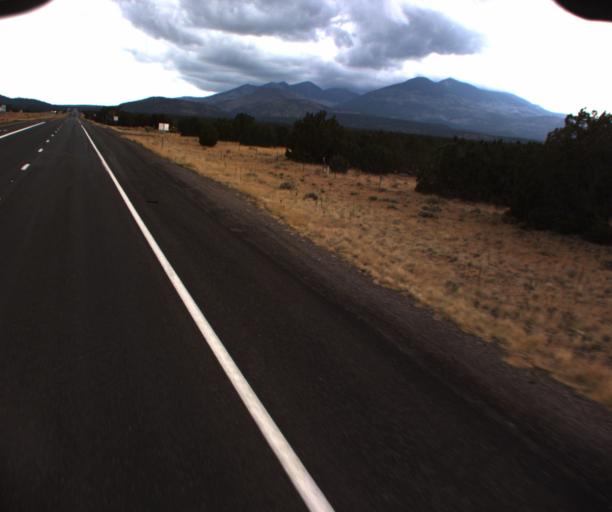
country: US
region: Arizona
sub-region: Coconino County
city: Flagstaff
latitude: 35.4288
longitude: -111.5690
